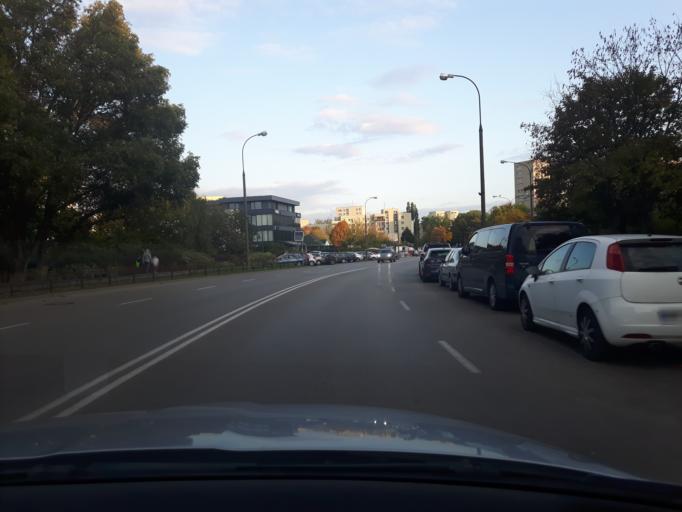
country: PL
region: Masovian Voivodeship
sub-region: Warszawa
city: Ursynow
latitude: 52.1558
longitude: 21.0275
